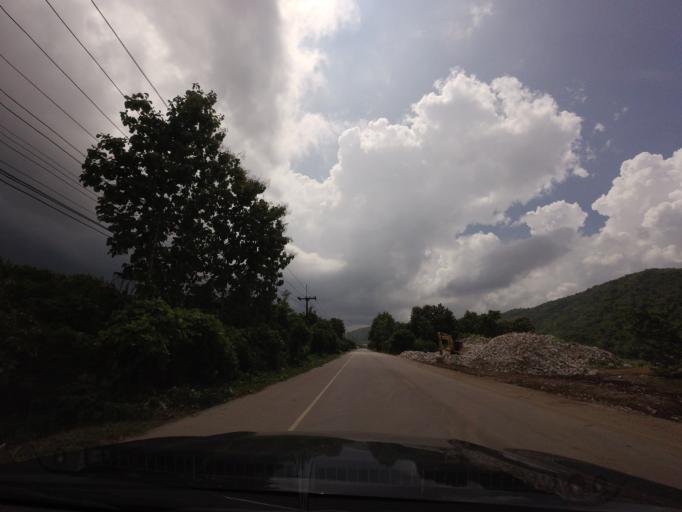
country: LA
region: Vientiane
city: Muang Sanakham
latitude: 17.9941
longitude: 101.7504
